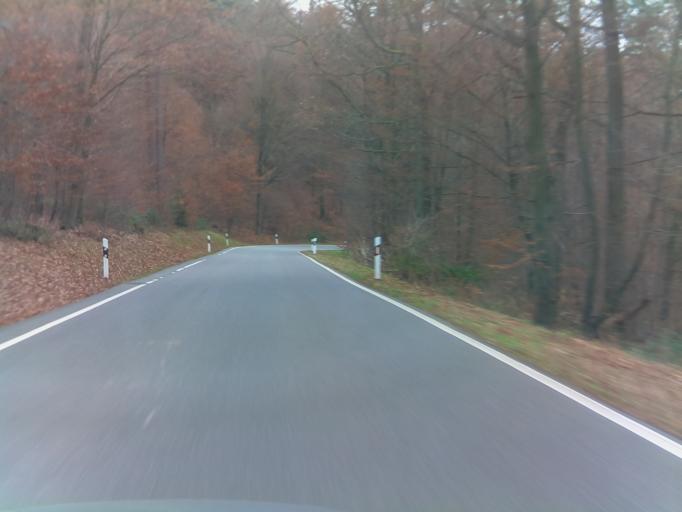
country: DE
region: Hesse
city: Hirschhorn
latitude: 49.4261
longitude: 8.9178
